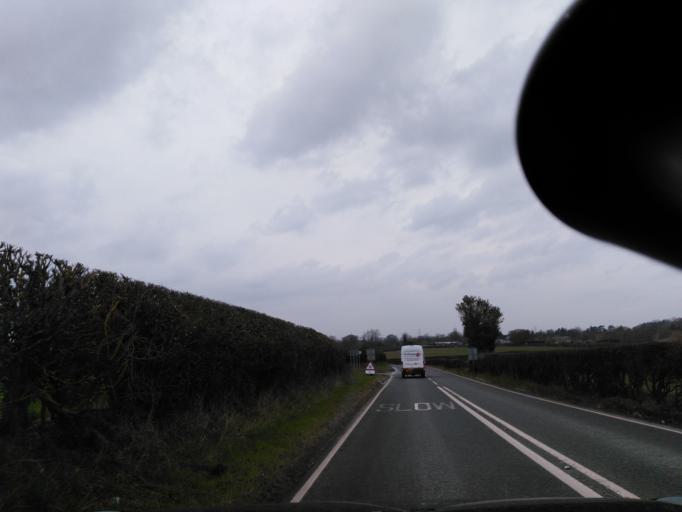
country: GB
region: England
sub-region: North Yorkshire
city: Angram Grange
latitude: 54.2348
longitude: -1.2450
